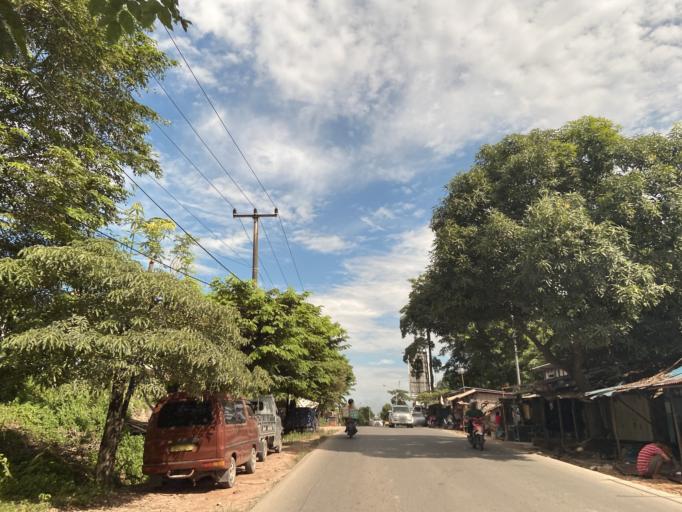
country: SG
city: Singapore
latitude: 1.0413
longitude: 103.9374
